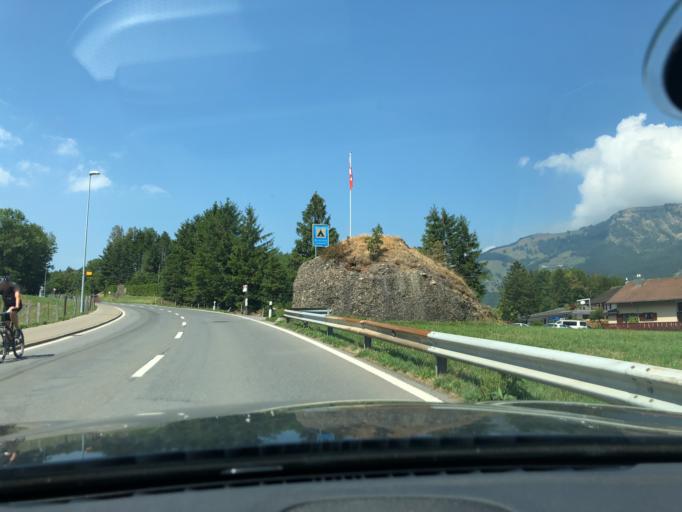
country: CH
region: Schwyz
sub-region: Bezirk Schwyz
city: Goldau
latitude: 47.0391
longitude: 8.5612
